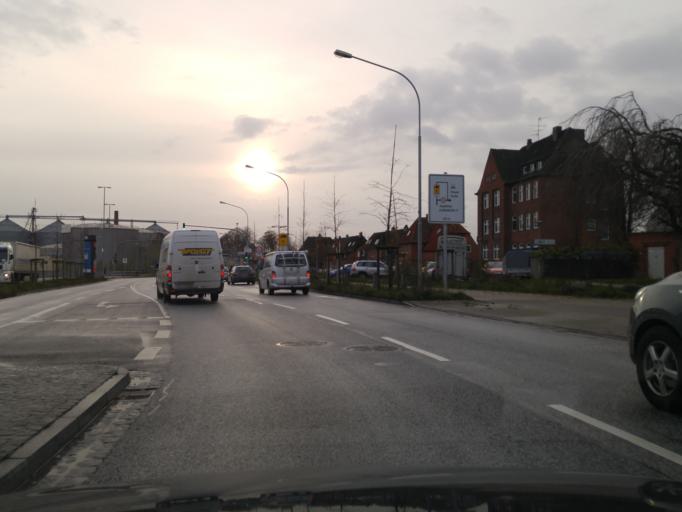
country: DE
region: Schleswig-Holstein
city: Luebeck
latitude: 53.8845
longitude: 10.6901
